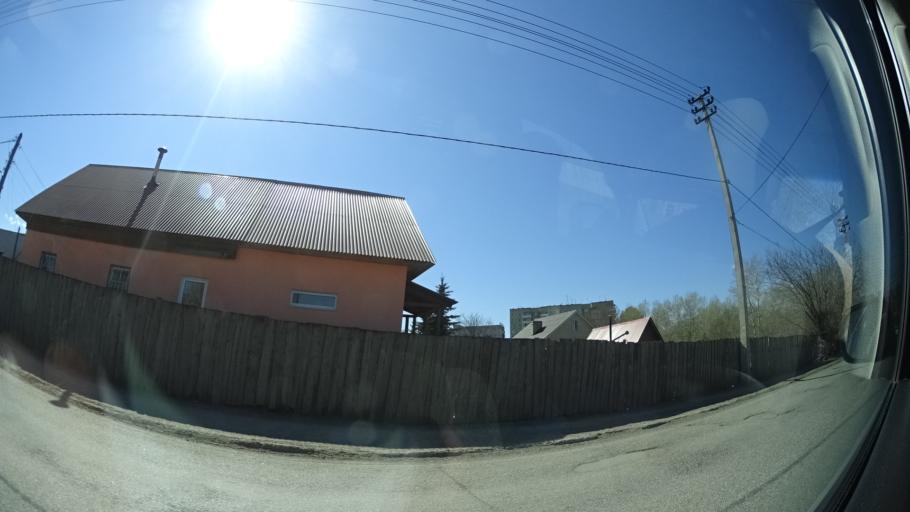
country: RU
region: Perm
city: Perm
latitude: 58.1166
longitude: 56.2940
